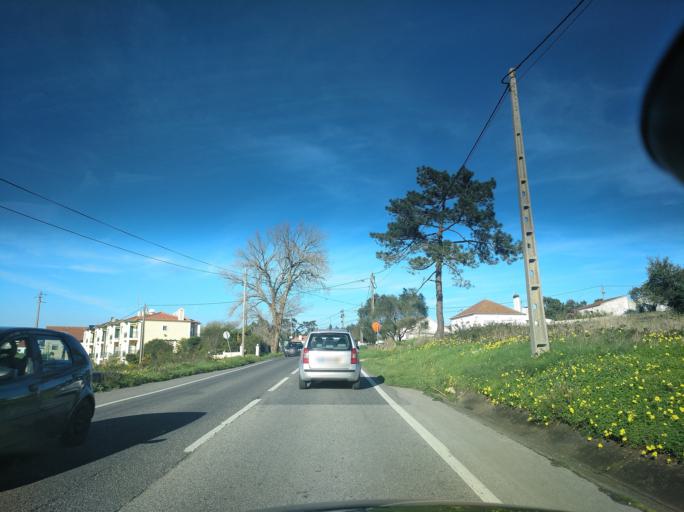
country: PT
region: Lisbon
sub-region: Mafra
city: Mafra
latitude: 38.9287
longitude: -9.3115
